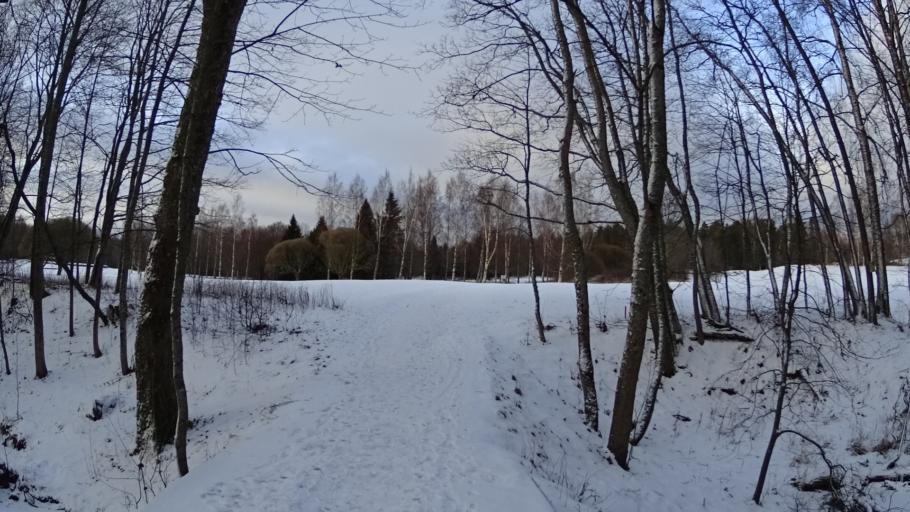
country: FI
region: Uusimaa
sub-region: Helsinki
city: Teekkarikylae
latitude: 60.2135
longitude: 24.8580
